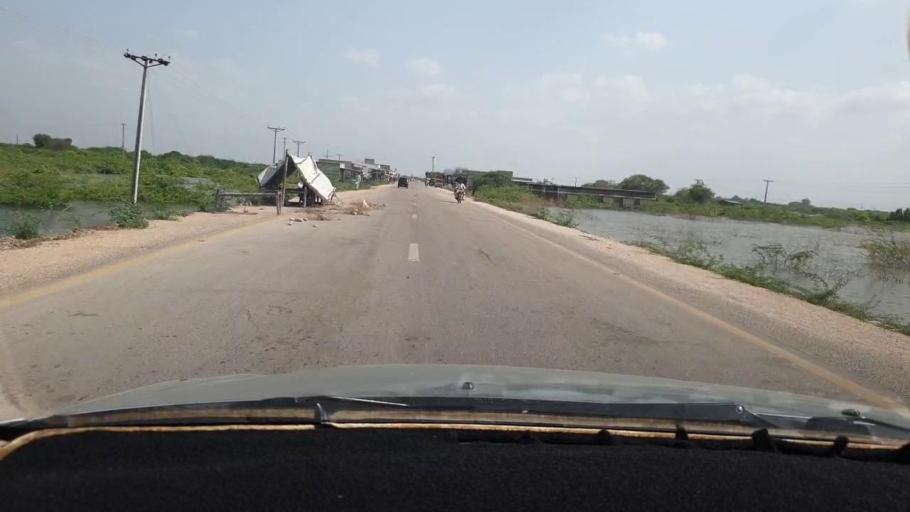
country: PK
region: Sindh
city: Naukot
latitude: 24.9044
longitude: 69.3293
